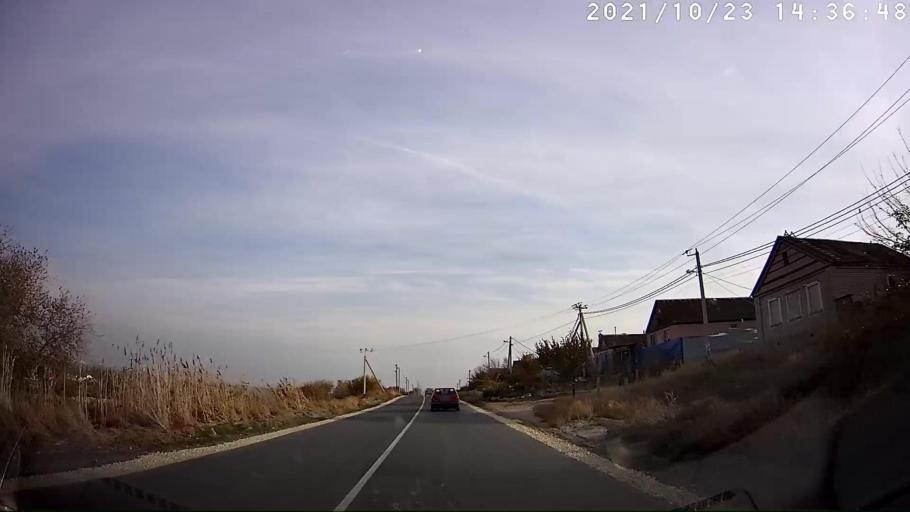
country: RU
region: Volgograd
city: Krasnoslobodsk
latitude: 48.5009
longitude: 44.5440
